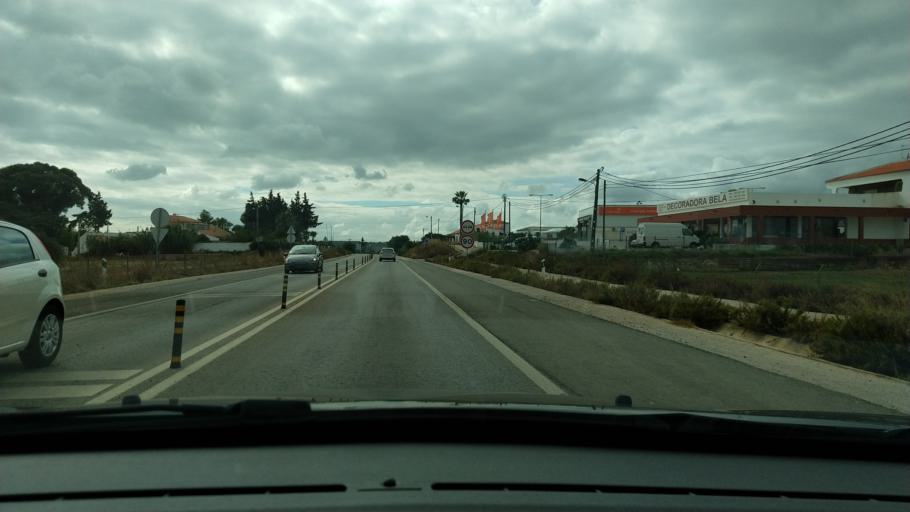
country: PT
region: Faro
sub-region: Lagos
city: Lagos
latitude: 37.0941
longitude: -8.7692
